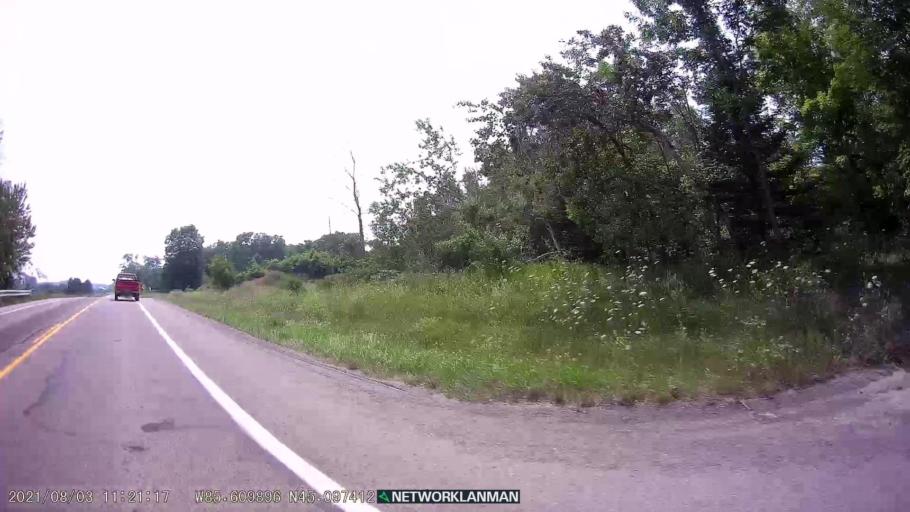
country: US
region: Michigan
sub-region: Leelanau County
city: Leland
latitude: 45.0973
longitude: -85.6100
